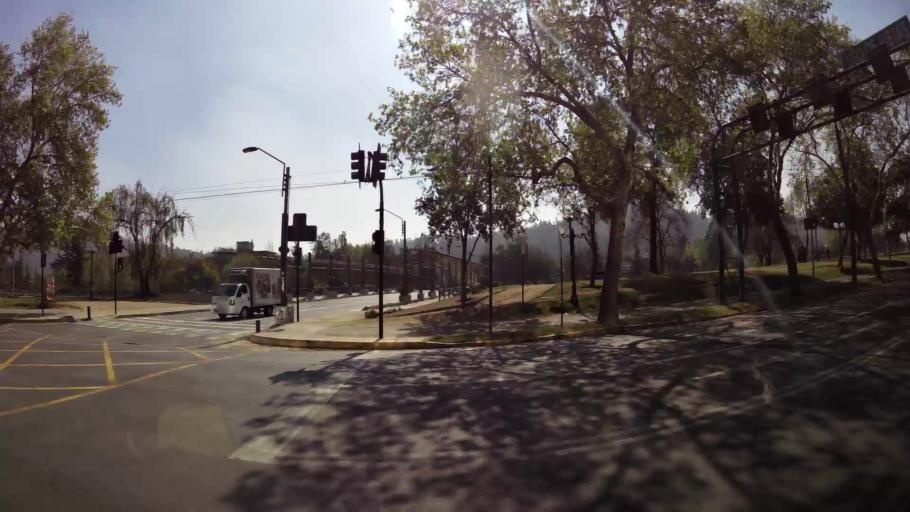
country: CL
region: Santiago Metropolitan
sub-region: Provincia de Santiago
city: Villa Presidente Frei, Nunoa, Santiago, Chile
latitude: -33.4187
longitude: -70.6092
